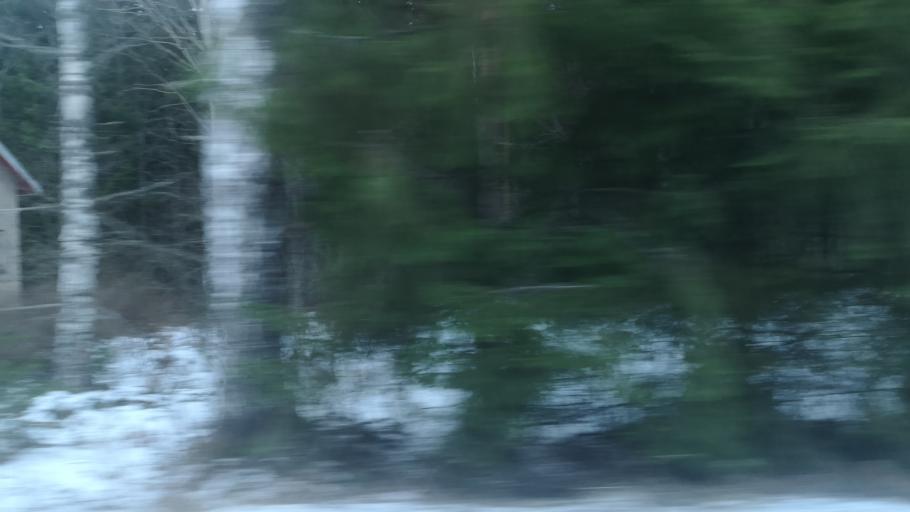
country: FI
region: Southern Savonia
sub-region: Savonlinna
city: Rantasalmi
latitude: 62.1167
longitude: 28.6101
